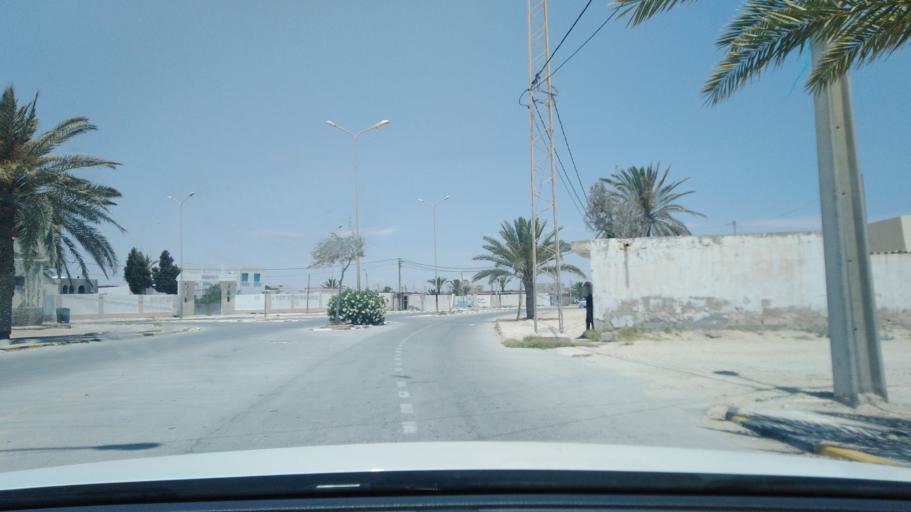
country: TN
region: Qabis
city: Gabes
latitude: 33.9486
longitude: 10.0699
